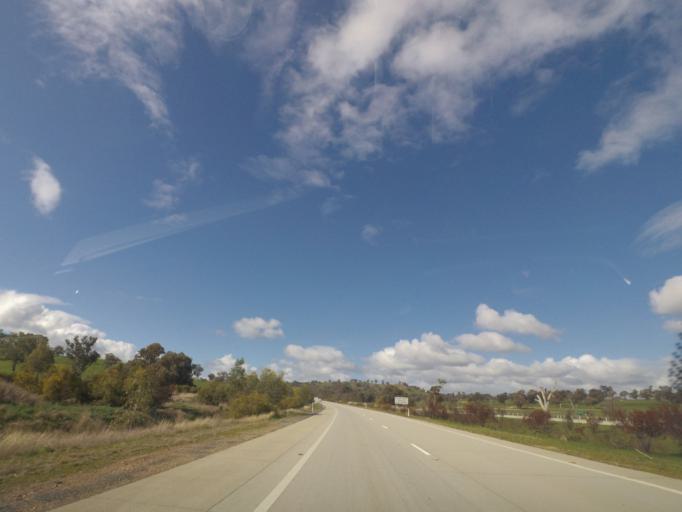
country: AU
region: New South Wales
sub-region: Albury Municipality
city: Lavington
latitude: -35.9269
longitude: 147.0806
